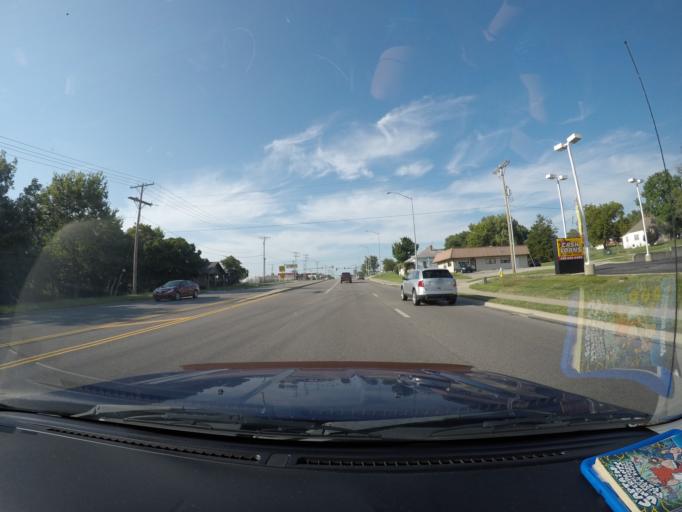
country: US
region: Kansas
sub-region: Leavenworth County
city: Lansing
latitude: 39.2654
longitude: -94.8998
